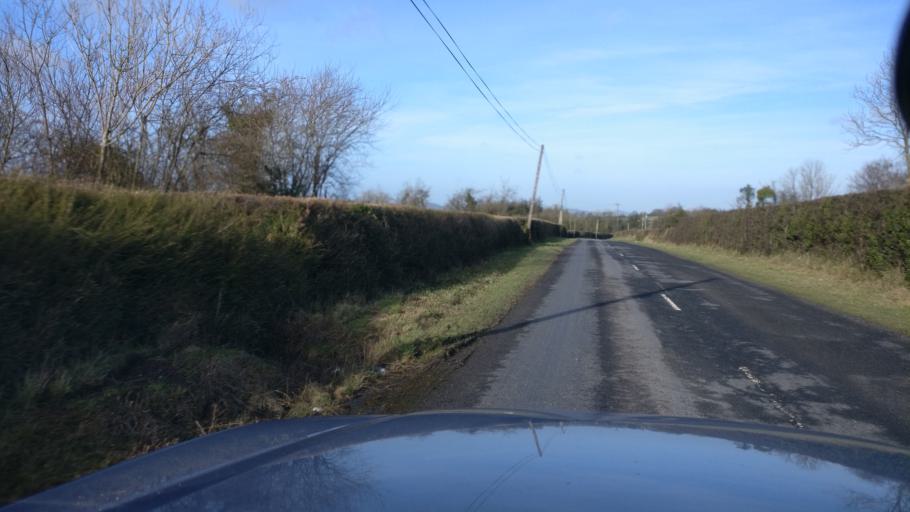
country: IE
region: Leinster
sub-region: Laois
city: Stradbally
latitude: 52.9315
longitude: -7.1983
